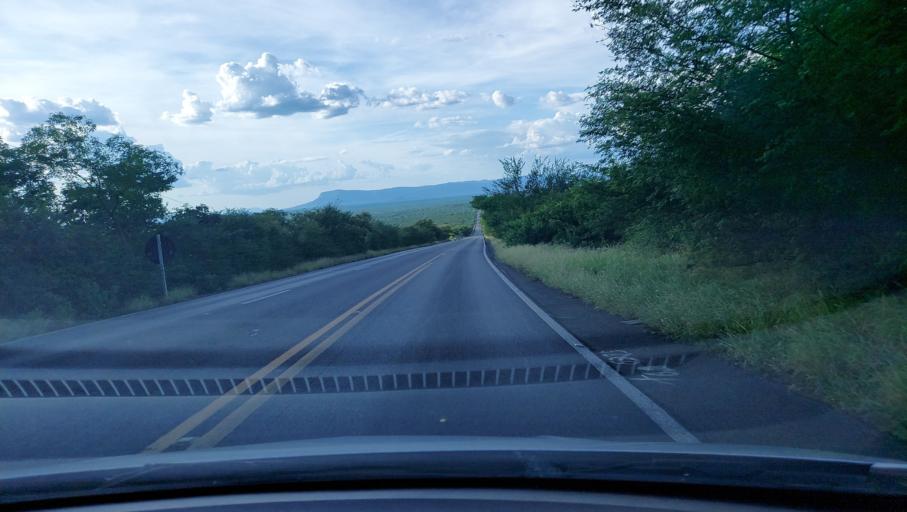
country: BR
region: Bahia
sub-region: Oliveira Dos Brejinhos
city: Beira Rio
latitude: -12.3992
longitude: -42.3961
